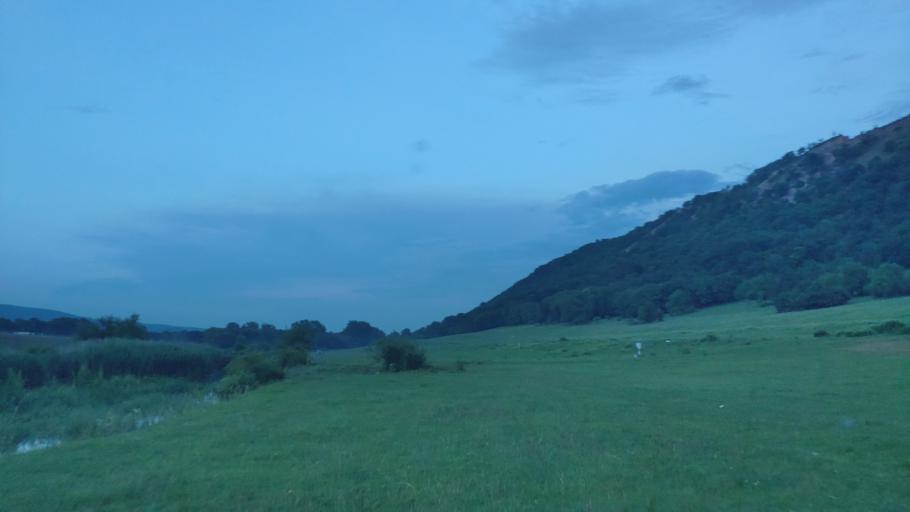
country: SK
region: Kosicky
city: Medzev
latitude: 48.5828
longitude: 20.8029
